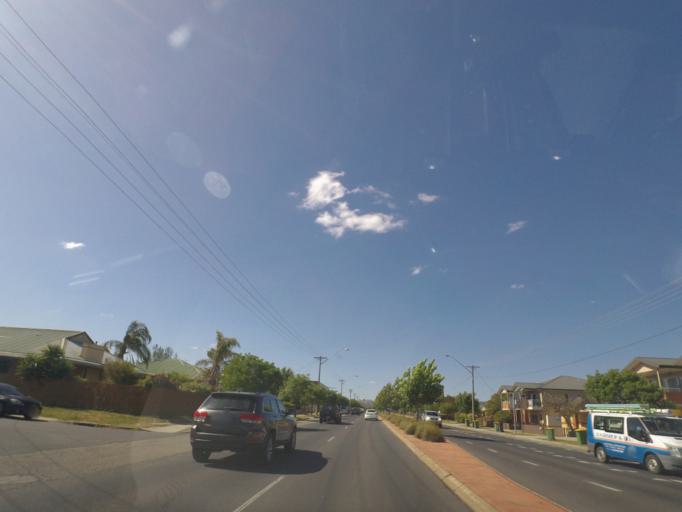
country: AU
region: New South Wales
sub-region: Albury Municipality
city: North Albury
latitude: -36.0624
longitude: 146.9316
